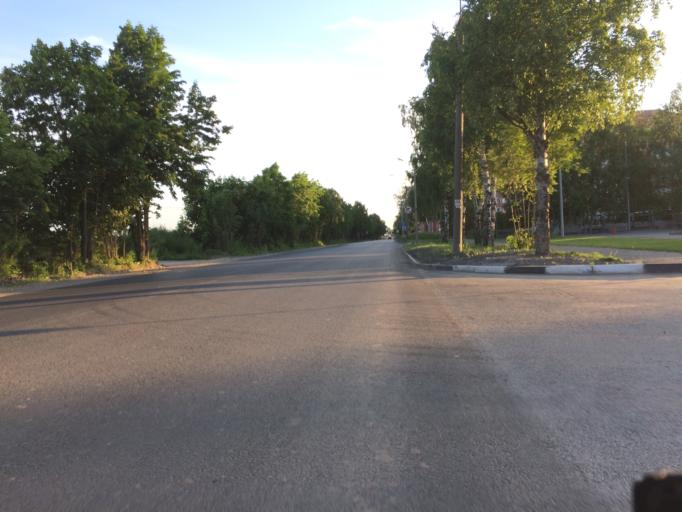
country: RU
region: Mariy-El
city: Medvedevo
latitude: 56.6430
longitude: 47.8316
